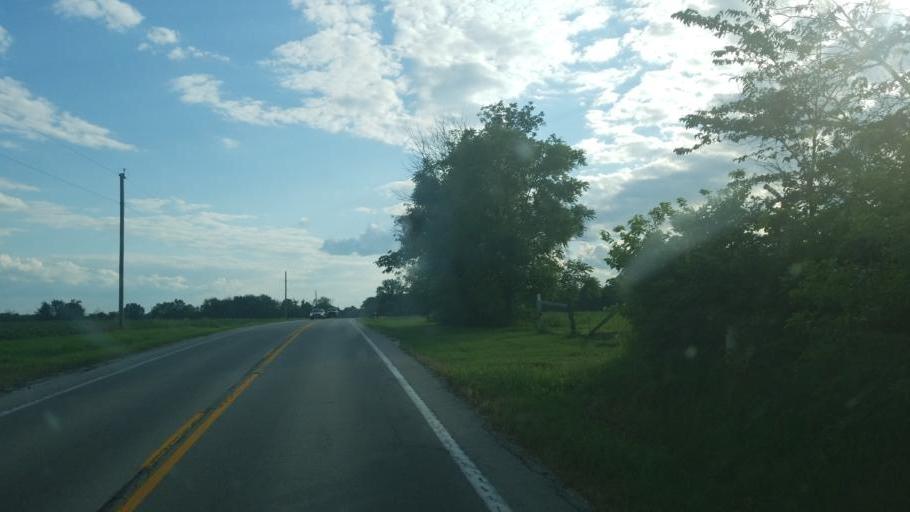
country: US
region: Ohio
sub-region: Seneca County
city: Tiffin
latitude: 41.1333
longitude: -83.1448
